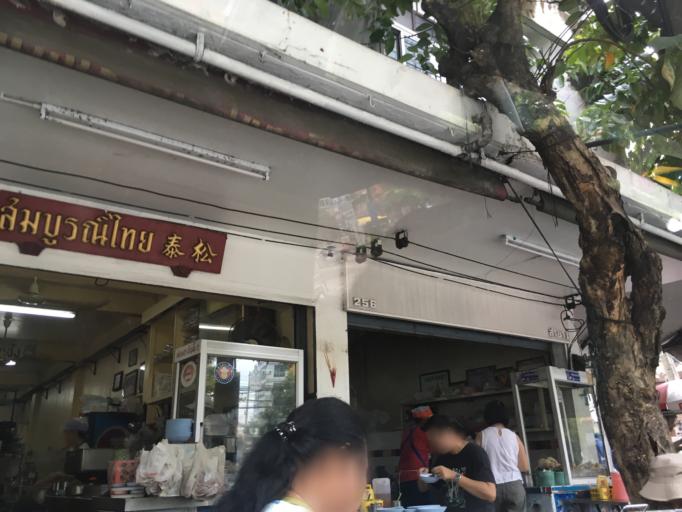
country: TH
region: Bangkok
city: Chatuchak
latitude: 13.8095
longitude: 100.5674
